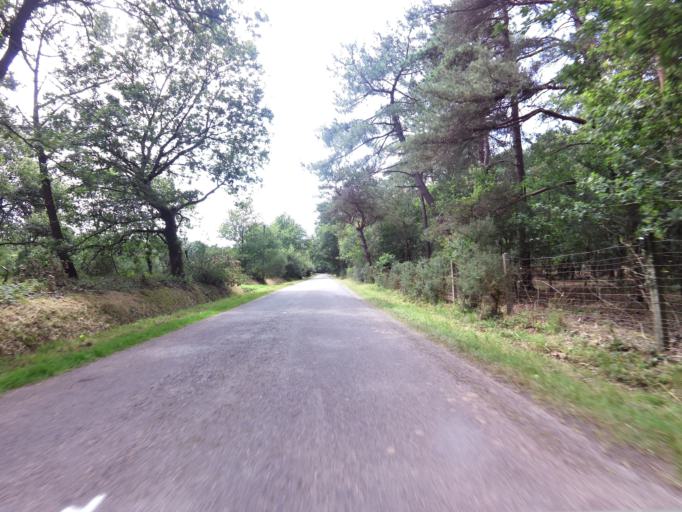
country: FR
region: Brittany
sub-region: Departement du Morbihan
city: Mauron
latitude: 48.0211
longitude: -2.2829
